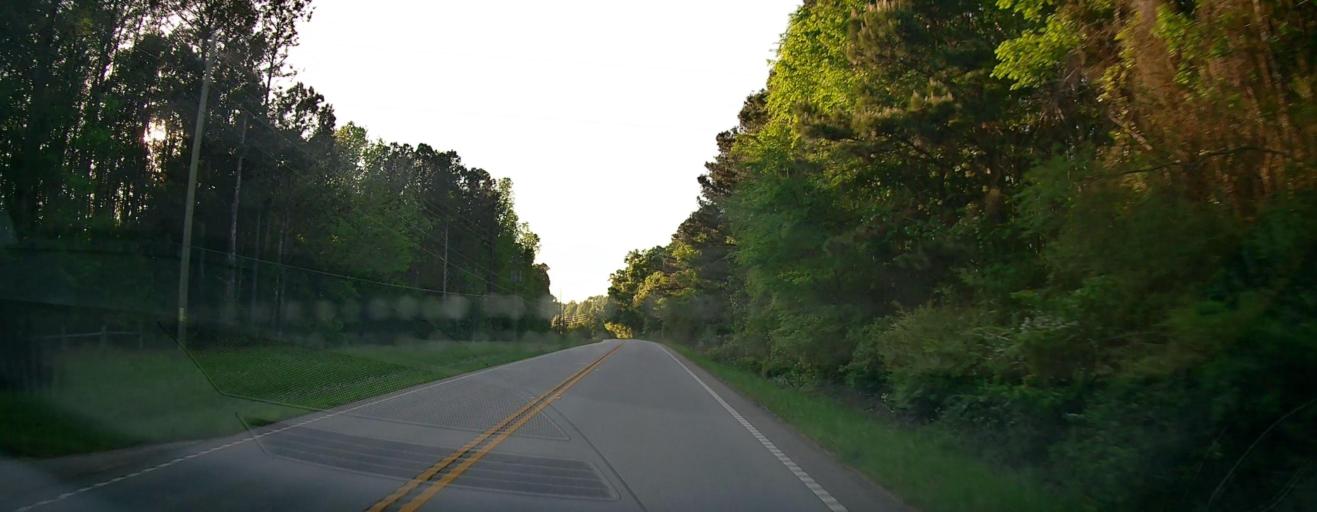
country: US
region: Georgia
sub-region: Walton County
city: Social Circle
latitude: 33.5629
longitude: -83.7532
